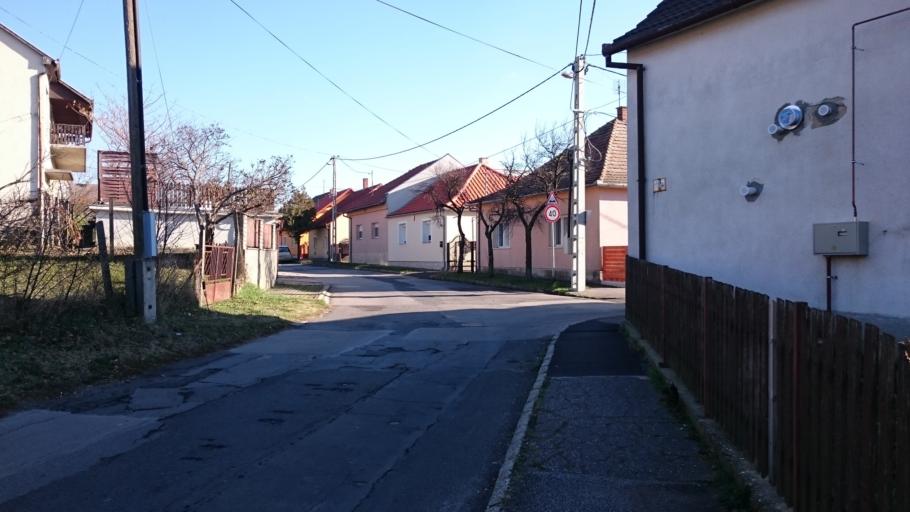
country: HU
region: Baranya
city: Pellerd
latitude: 46.0680
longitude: 18.1741
